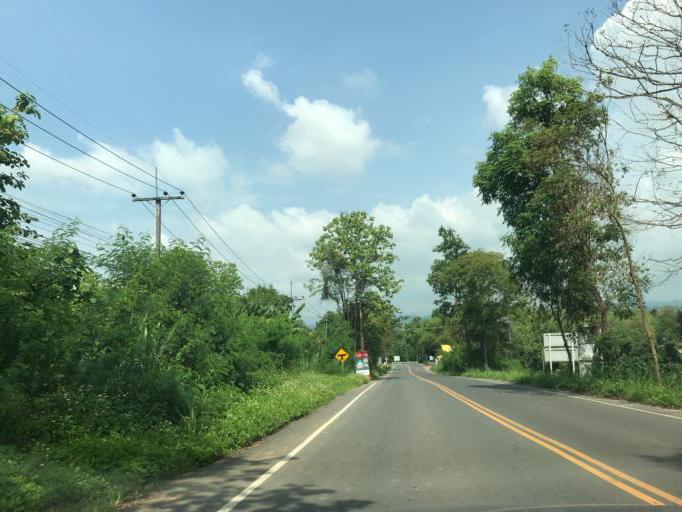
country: TH
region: Phayao
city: Pong
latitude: 19.1843
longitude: 100.2799
